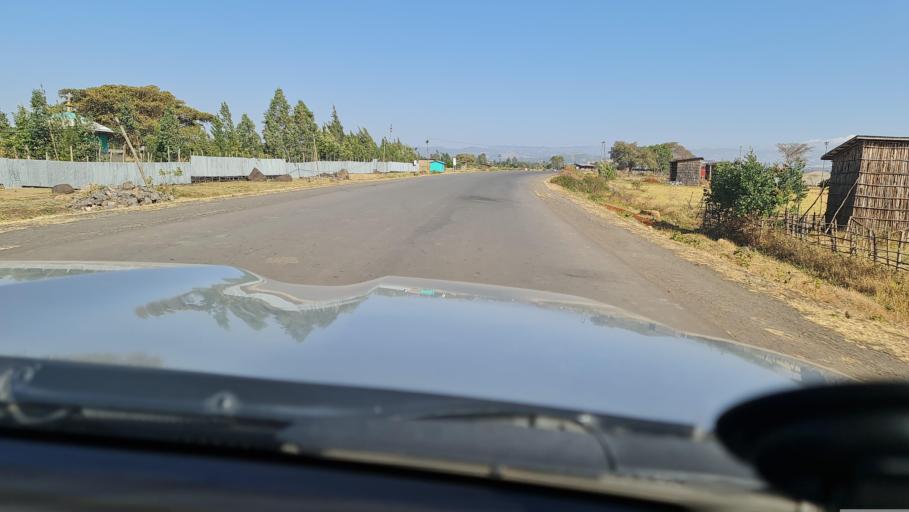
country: ET
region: Oromiya
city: Waliso
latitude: 8.5560
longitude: 37.9499
